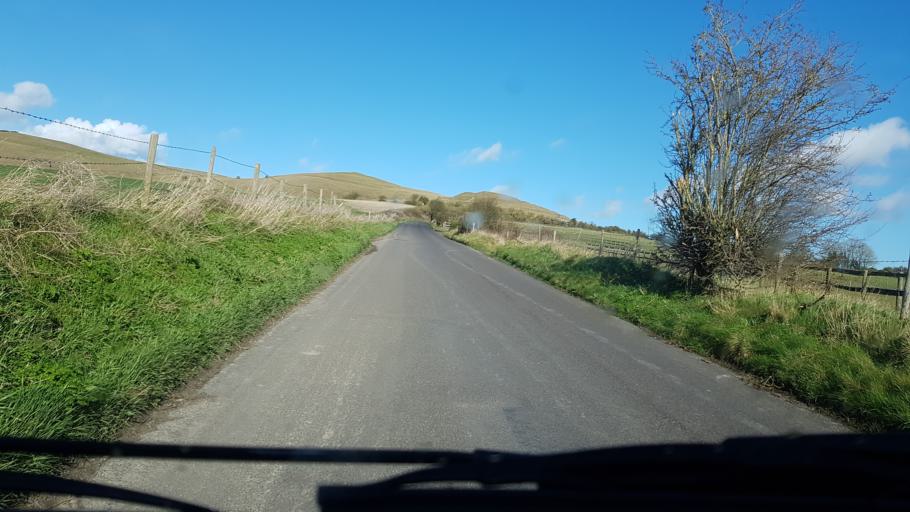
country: GB
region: England
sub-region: Wiltshire
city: Woodborough
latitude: 51.3624
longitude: -1.8468
